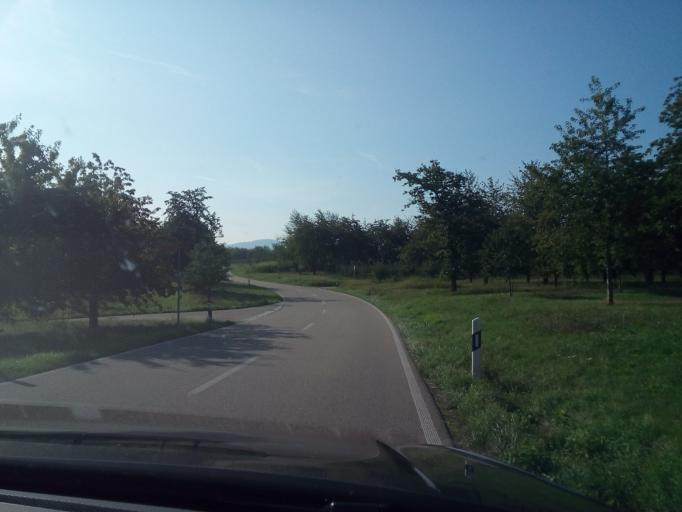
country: DE
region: Baden-Wuerttemberg
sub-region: Freiburg Region
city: Haslach
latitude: 48.5641
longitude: 8.0436
